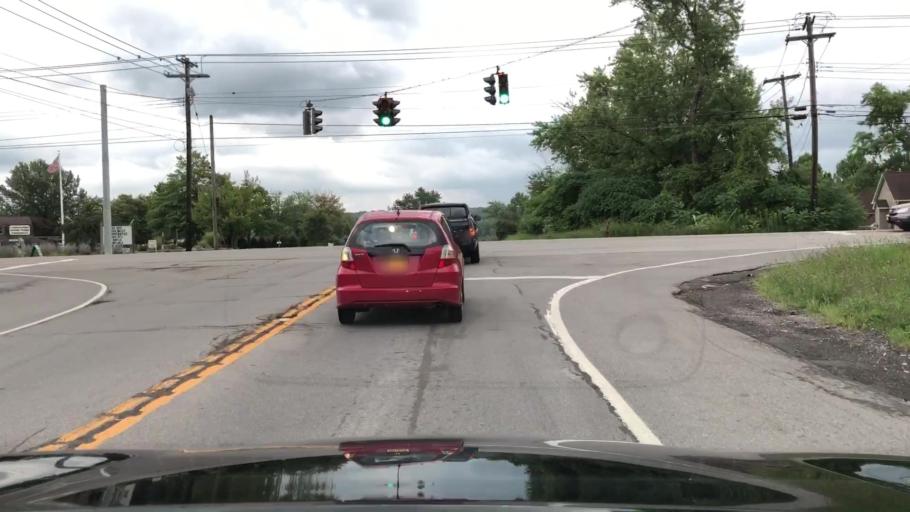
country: US
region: New York
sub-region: Erie County
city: Orchard Park
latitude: 42.7690
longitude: -78.6969
